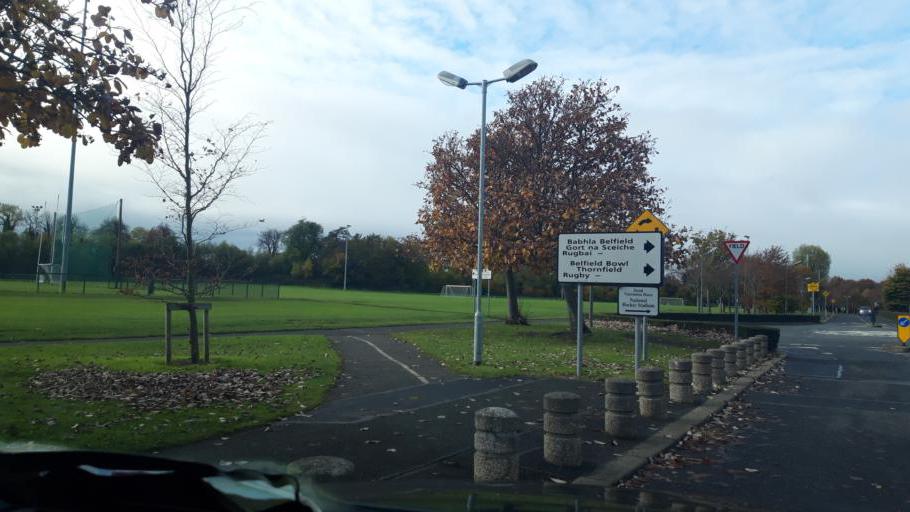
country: IE
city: Clonskeagh
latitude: 53.3079
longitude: -6.2297
